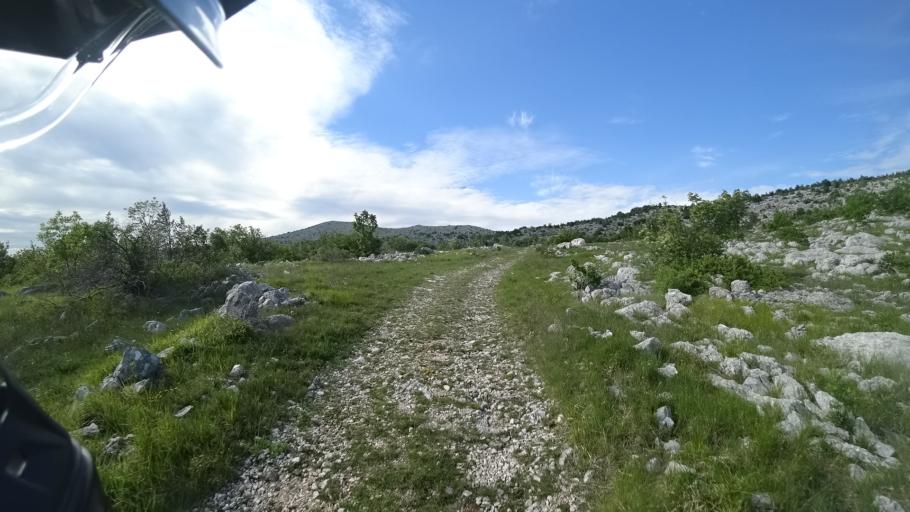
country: HR
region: Splitsko-Dalmatinska
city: Hrvace
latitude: 43.7953
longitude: 16.4337
